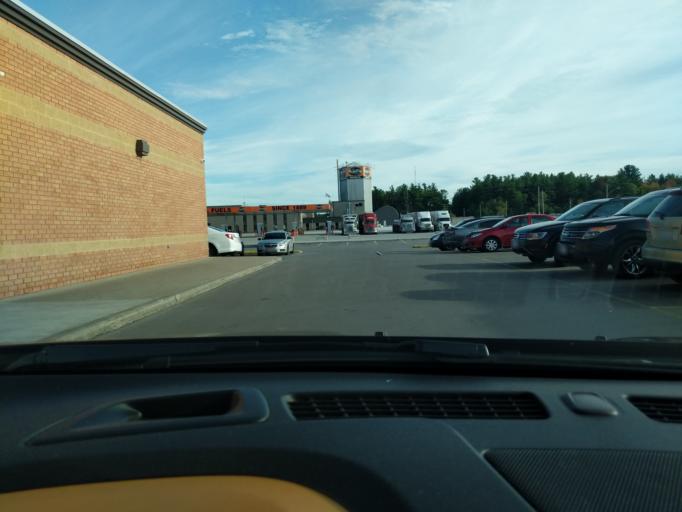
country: CA
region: Ontario
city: Barrie
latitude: 44.3773
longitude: -79.7157
